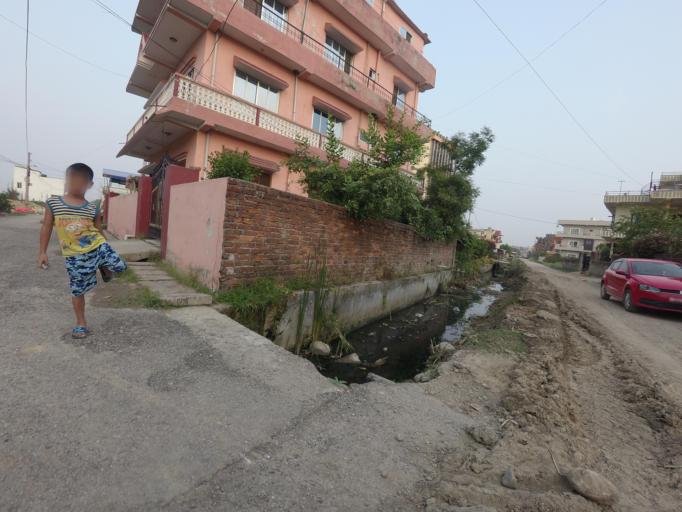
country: NP
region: Western Region
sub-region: Lumbini Zone
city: Bhairahawa
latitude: 27.5153
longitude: 83.4603
